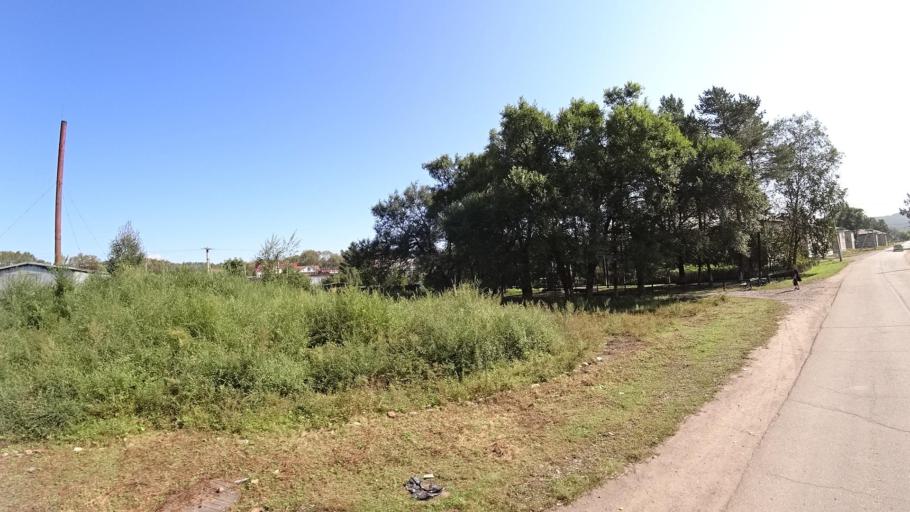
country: RU
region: Jewish Autonomous Oblast
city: Bira
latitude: 48.9983
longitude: 132.4618
